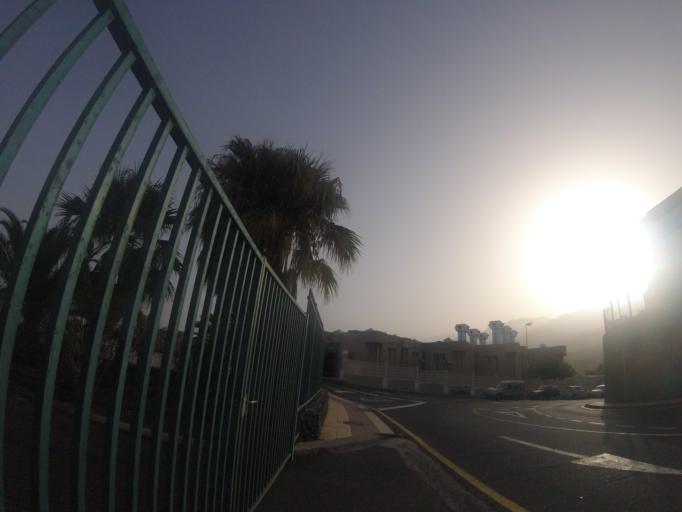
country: ES
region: Canary Islands
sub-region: Provincia de Santa Cruz de Tenerife
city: Candelaria
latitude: 28.4013
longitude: -16.3199
